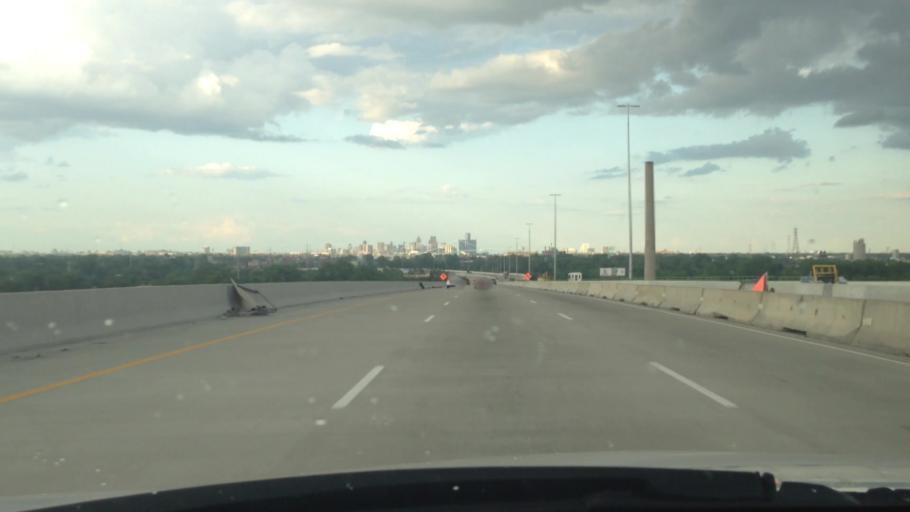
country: US
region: Michigan
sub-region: Wayne County
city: River Rouge
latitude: 42.2874
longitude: -83.1386
